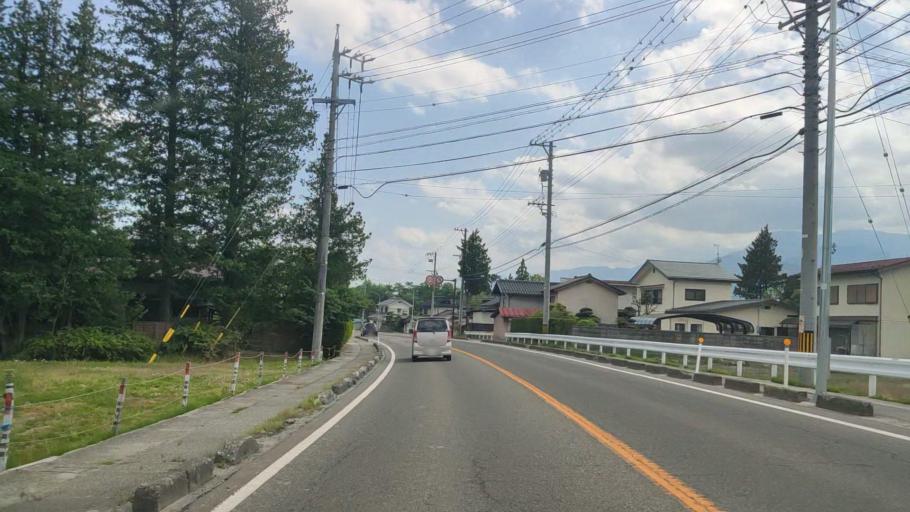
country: JP
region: Nagano
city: Omachi
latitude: 36.4750
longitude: 137.8482
